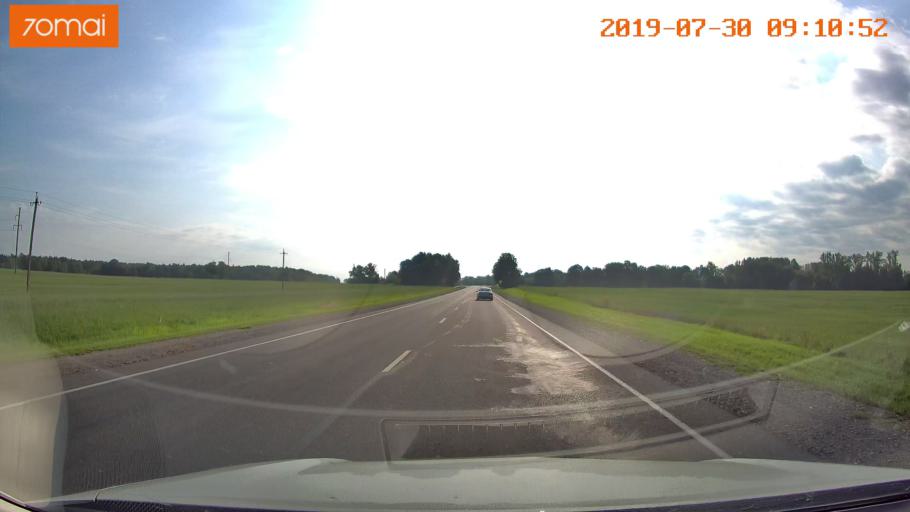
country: RU
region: Kaliningrad
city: Nesterov
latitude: 54.6120
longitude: 22.4376
